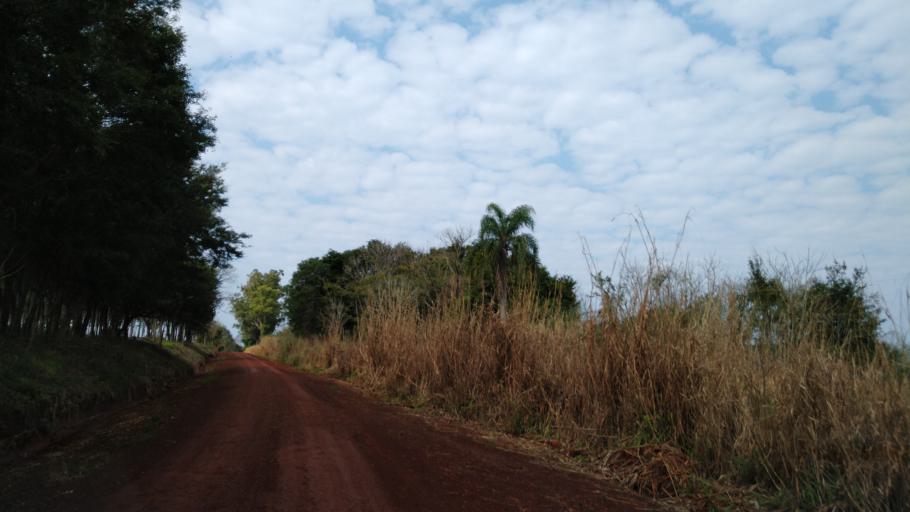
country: AR
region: Misiones
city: Capiovi
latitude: -26.9513
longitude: -55.0666
